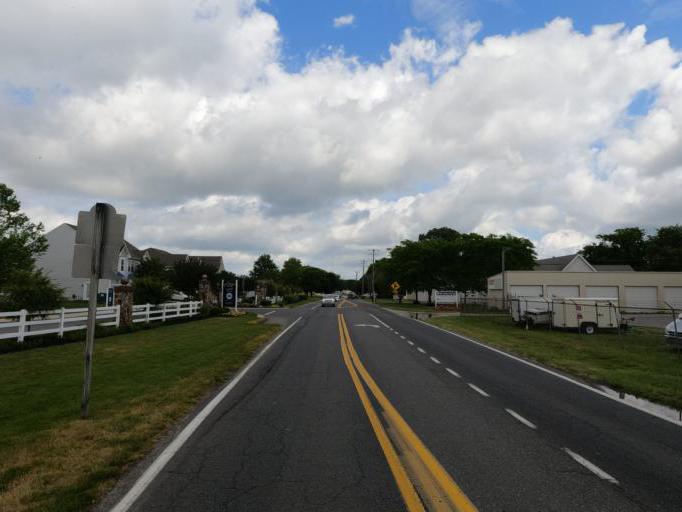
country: US
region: Delaware
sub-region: Sussex County
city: Lewes
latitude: 38.7228
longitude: -75.1313
